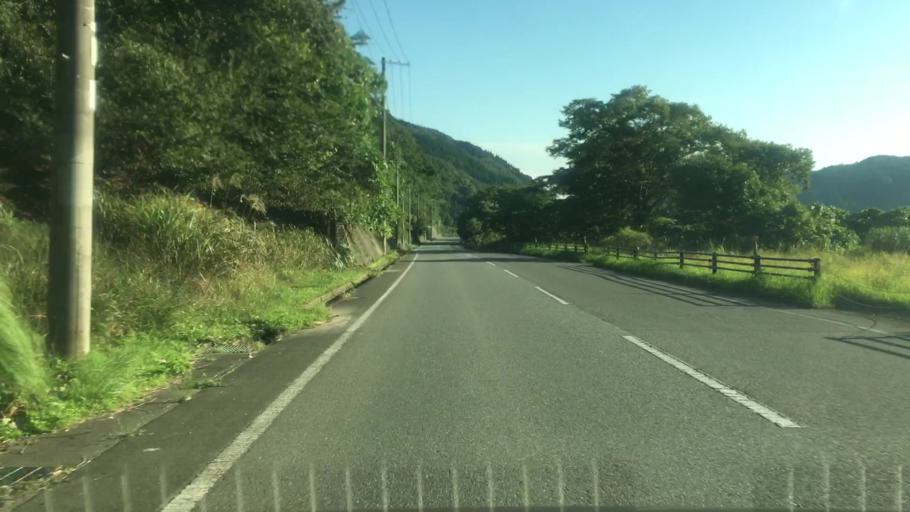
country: JP
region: Hyogo
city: Toyooka
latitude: 35.6021
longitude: 134.8059
